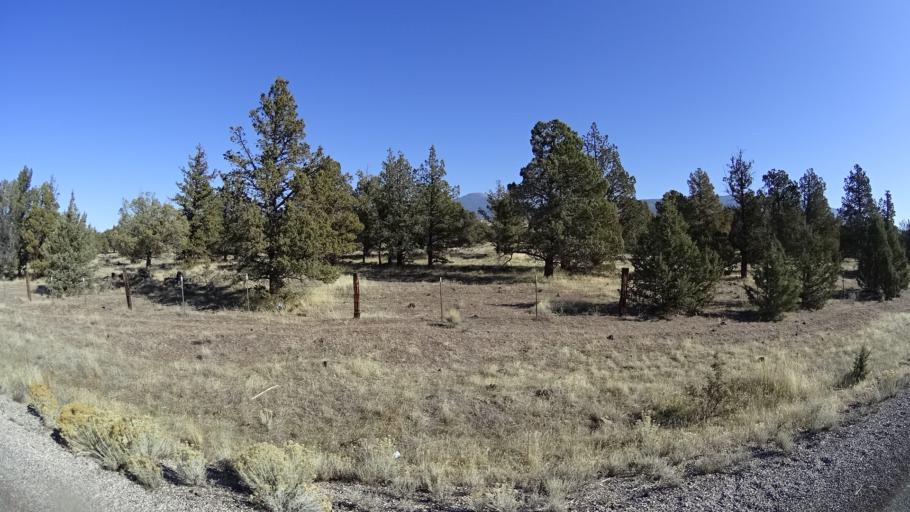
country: US
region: California
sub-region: Siskiyou County
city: Montague
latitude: 41.6620
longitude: -122.3686
